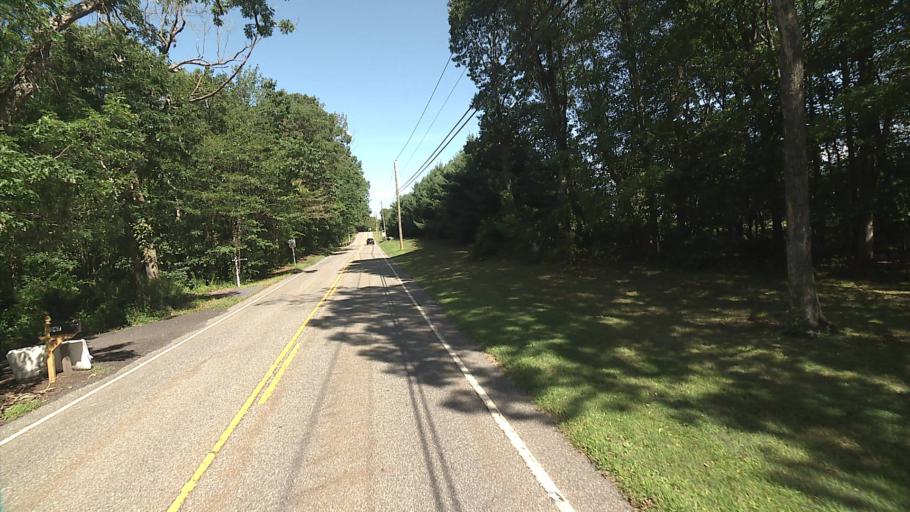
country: US
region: Connecticut
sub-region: Litchfield County
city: Northwest Harwinton
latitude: 41.7511
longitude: -73.0808
